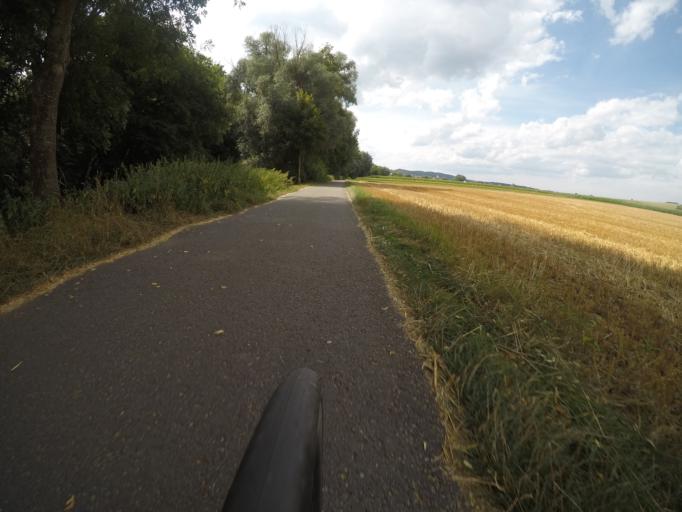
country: DE
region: Baden-Wuerttemberg
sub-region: Regierungsbezirk Stuttgart
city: Weil der Stadt
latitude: 48.7615
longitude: 8.8688
